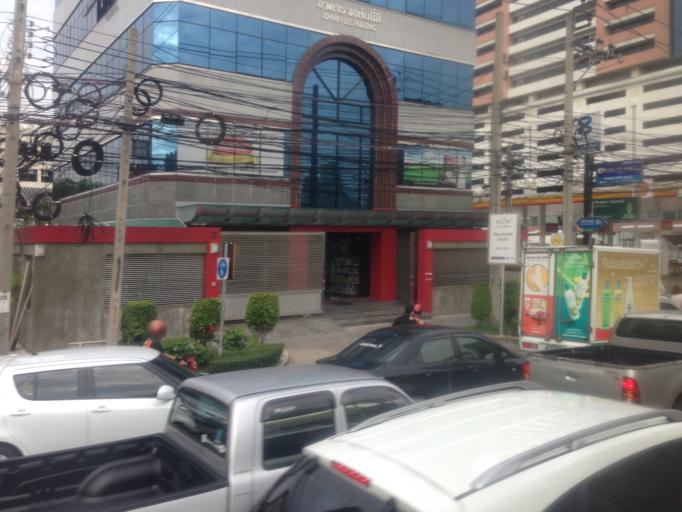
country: TH
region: Bangkok
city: Sathon
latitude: 13.7159
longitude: 100.5331
